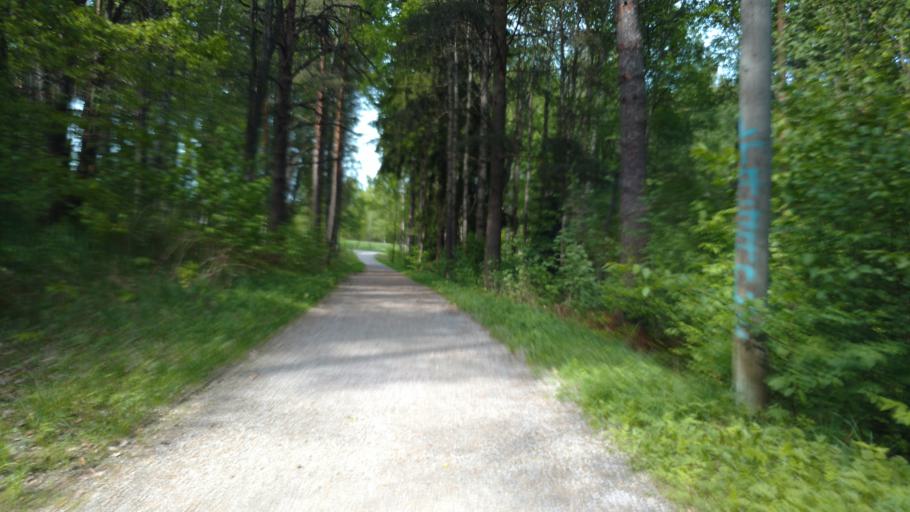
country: FI
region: Varsinais-Suomi
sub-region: Salo
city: Halikko
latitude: 60.3909
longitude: 23.1014
